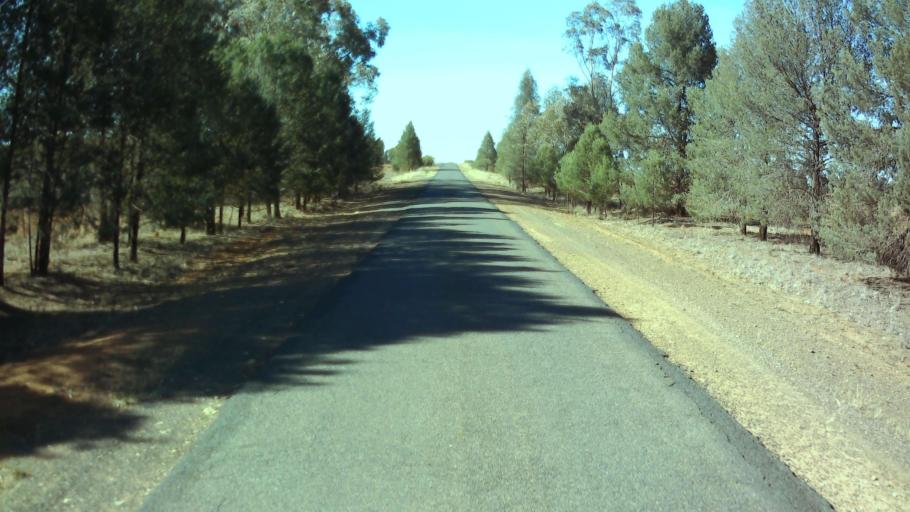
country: AU
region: New South Wales
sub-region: Weddin
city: Grenfell
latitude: -33.7578
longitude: 147.8300
